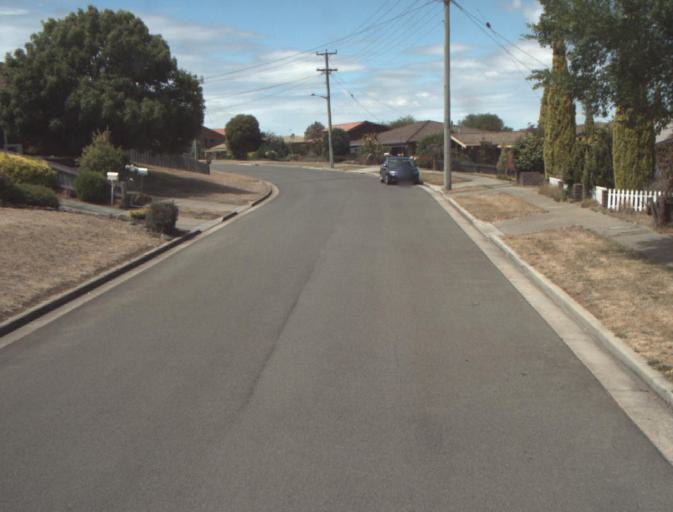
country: AU
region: Tasmania
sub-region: Launceston
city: Mayfield
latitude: -41.3801
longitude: 147.1160
